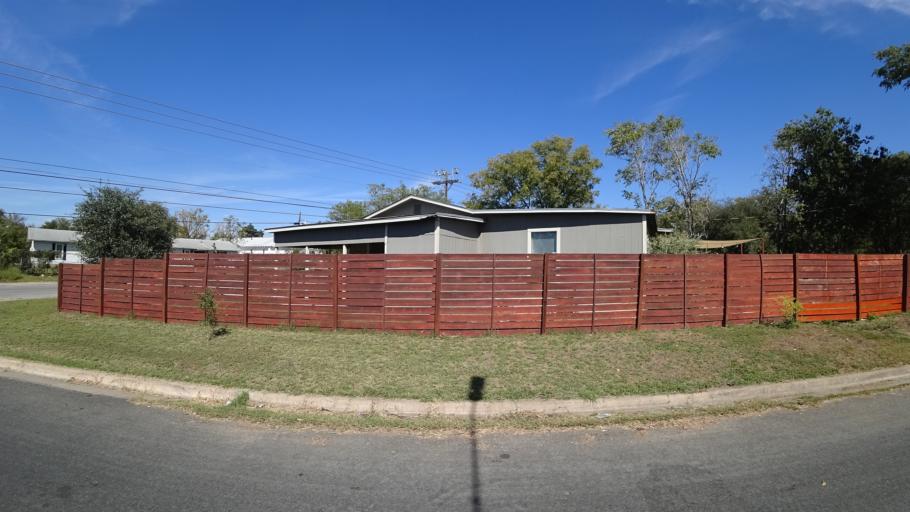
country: US
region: Texas
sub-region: Travis County
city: Austin
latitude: 30.2767
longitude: -97.6868
